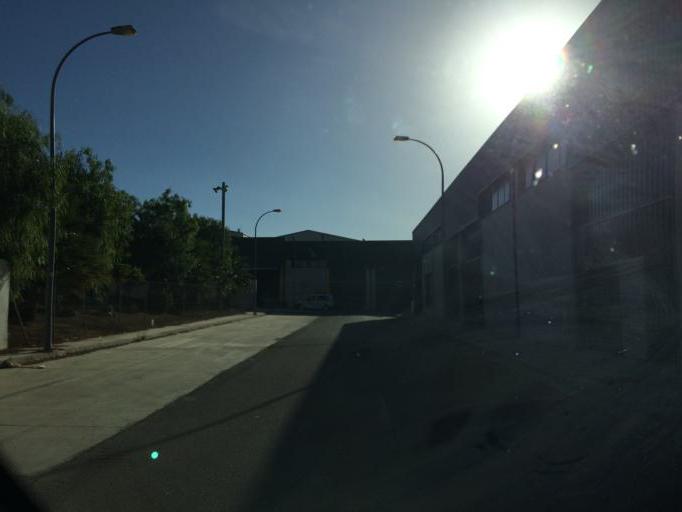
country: ES
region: Andalusia
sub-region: Provincia de Malaga
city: Campillos
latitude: 37.0500
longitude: -4.8758
